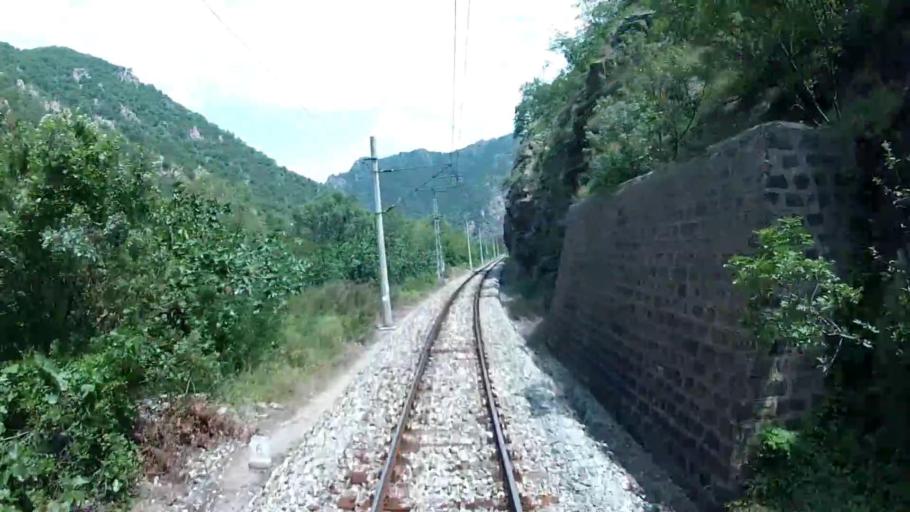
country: BG
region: Blagoevgrad
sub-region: Obshtina Kresna
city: Stara Kresna
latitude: 41.8049
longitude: 23.1637
